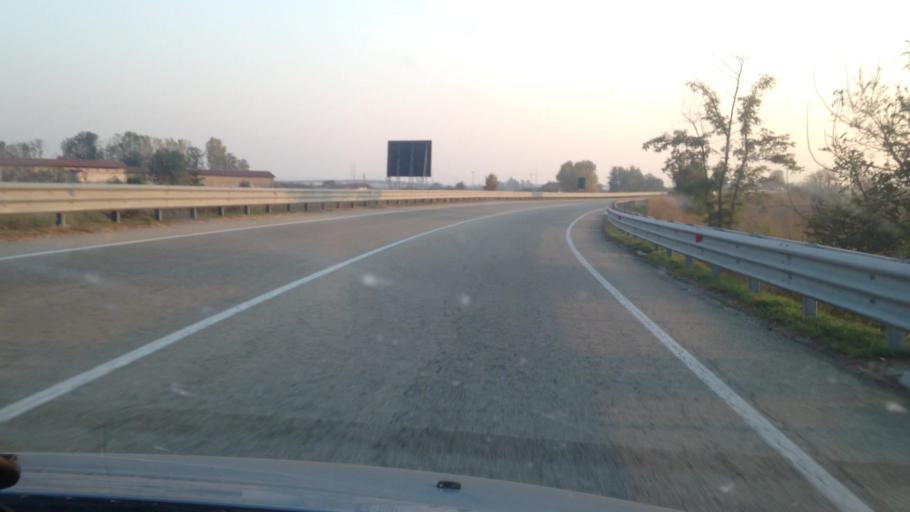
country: IT
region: Piedmont
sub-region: Provincia di Vercelli
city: Cigliano
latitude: 45.3104
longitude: 8.0417
